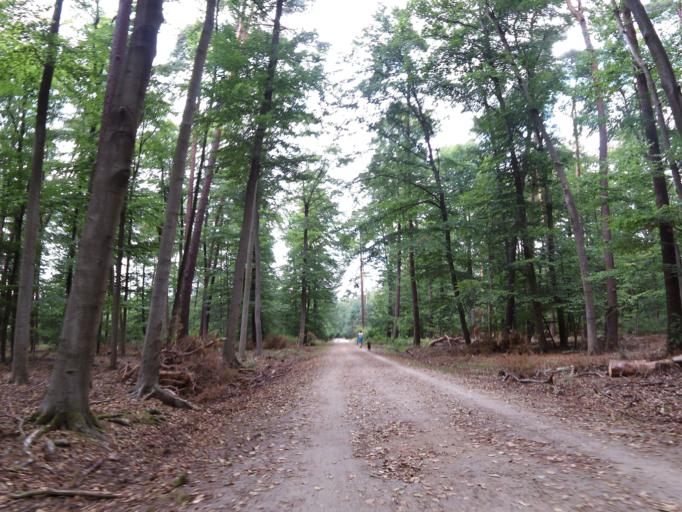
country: DE
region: Hesse
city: Morfelden-Walldorf
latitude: 49.9976
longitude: 8.5592
